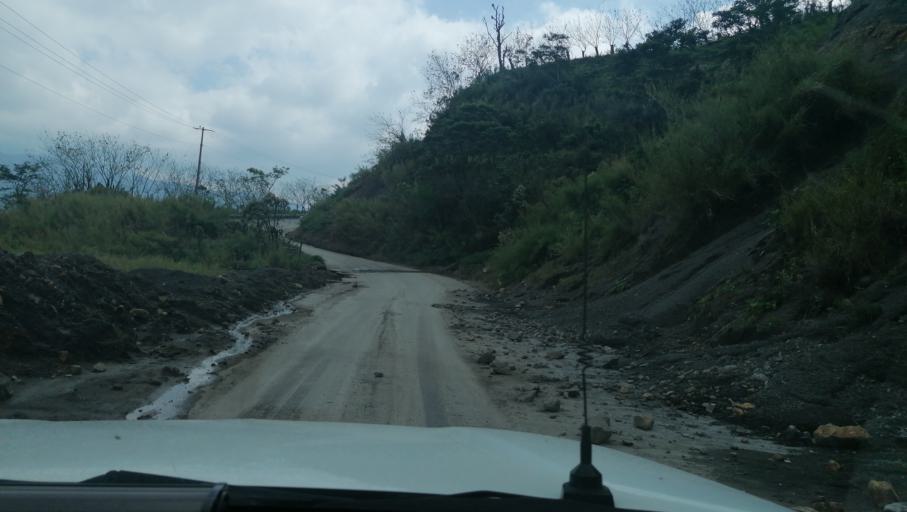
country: MX
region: Chiapas
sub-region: Ocotepec
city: San Pablo Huacano
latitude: 17.2649
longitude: -93.2648
